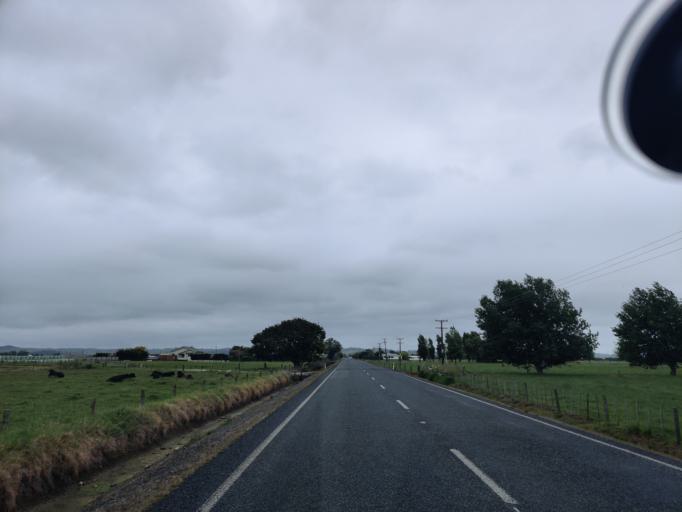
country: NZ
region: Northland
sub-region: Kaipara District
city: Dargaville
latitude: -36.1276
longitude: 174.0387
